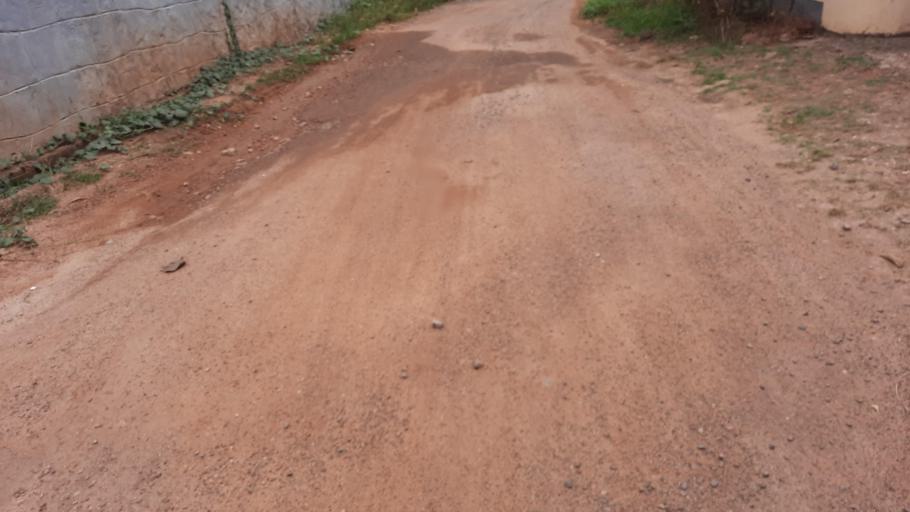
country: IN
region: Kerala
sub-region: Thiruvananthapuram
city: Thiruvananthapuram
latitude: 8.5599
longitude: 76.9313
